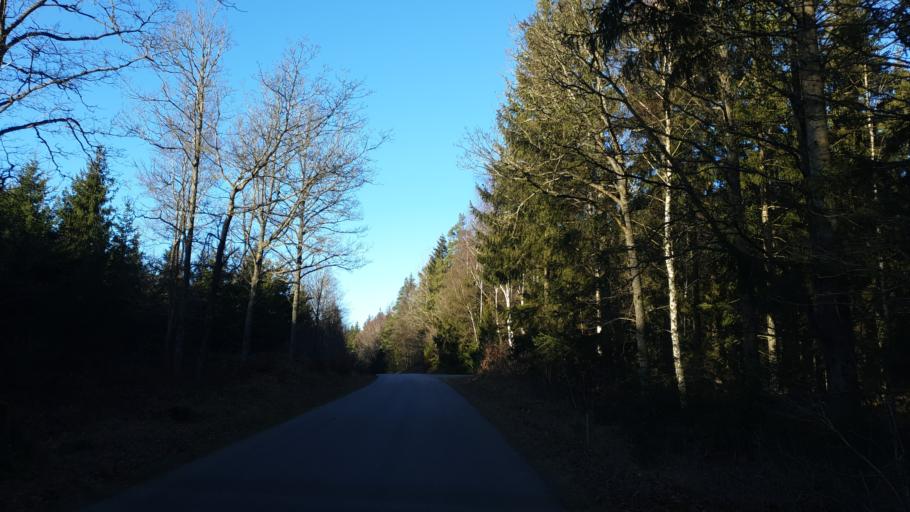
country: SE
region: Blekinge
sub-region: Karlskrona Kommun
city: Nattraby
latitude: 56.2639
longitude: 15.4821
